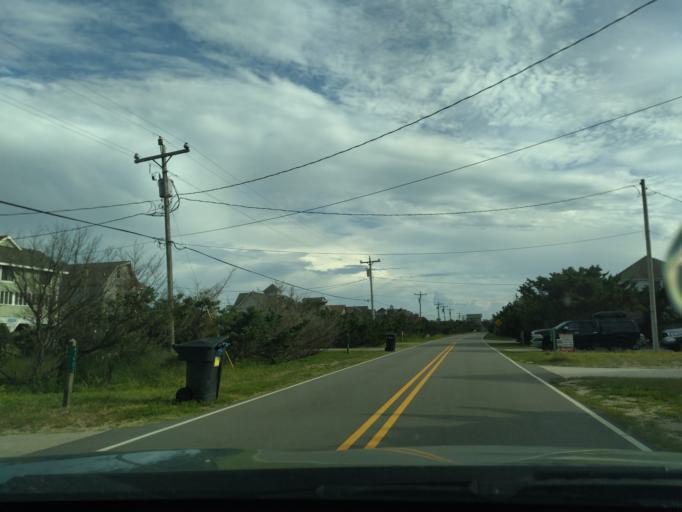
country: US
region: North Carolina
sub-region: Dare County
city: Buxton
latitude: 35.3341
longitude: -75.5056
